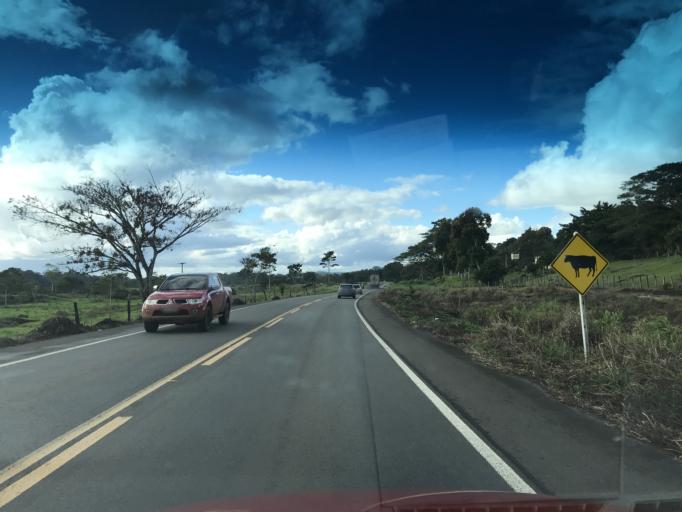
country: BR
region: Bahia
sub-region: Ibirapitanga
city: Ibirapitanga
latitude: -14.1622
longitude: -39.3287
